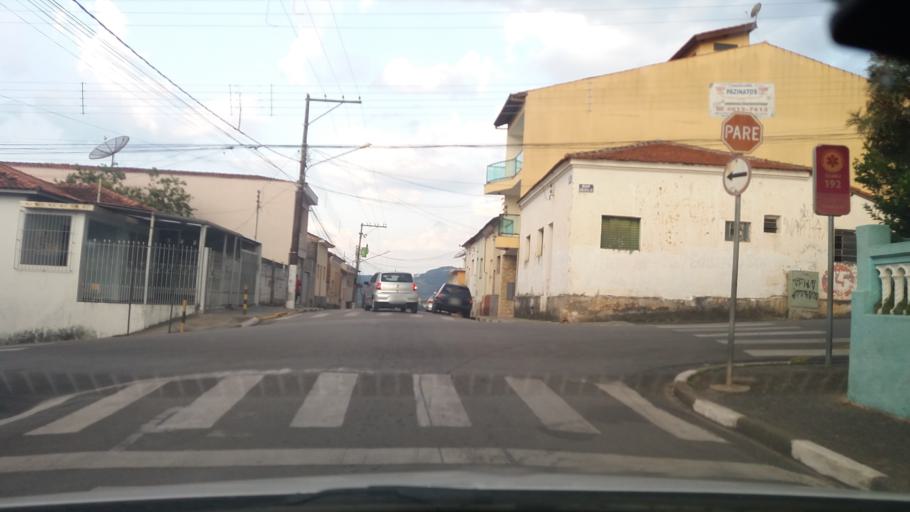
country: BR
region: Sao Paulo
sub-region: Bom Jesus Dos Perdoes
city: Bom Jesus dos Perdoes
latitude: -23.1369
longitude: -46.4651
